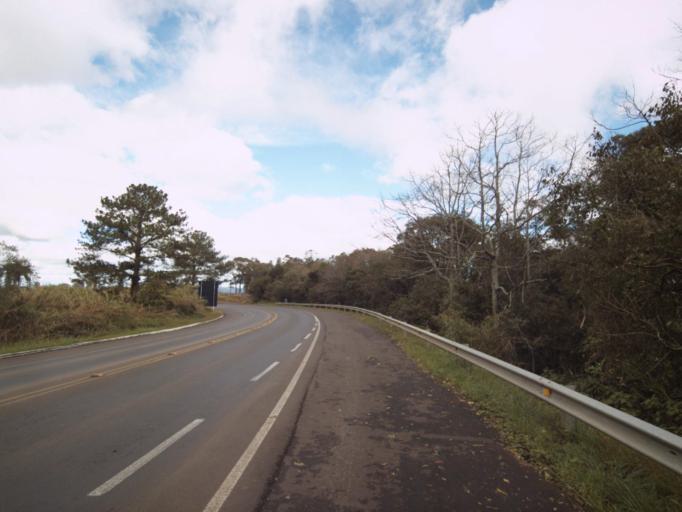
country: BR
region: Santa Catarina
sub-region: Concordia
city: Concordia
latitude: -27.3167
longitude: -51.9872
